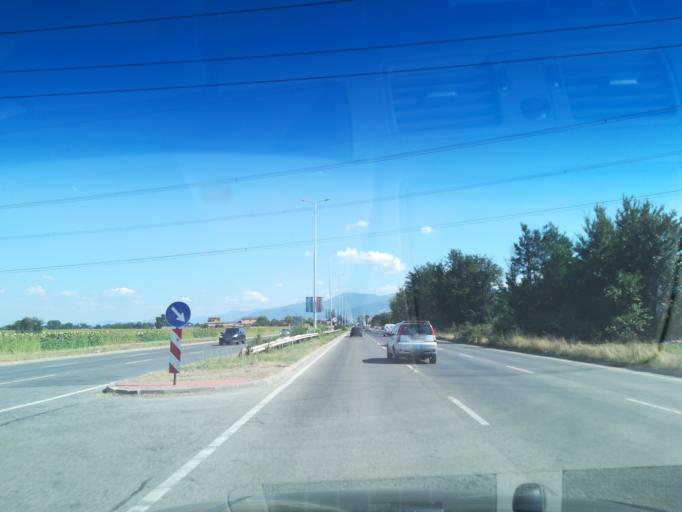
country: BG
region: Plovdiv
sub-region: Obshtina Plovdiv
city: Plovdiv
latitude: 42.1089
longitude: 24.7817
